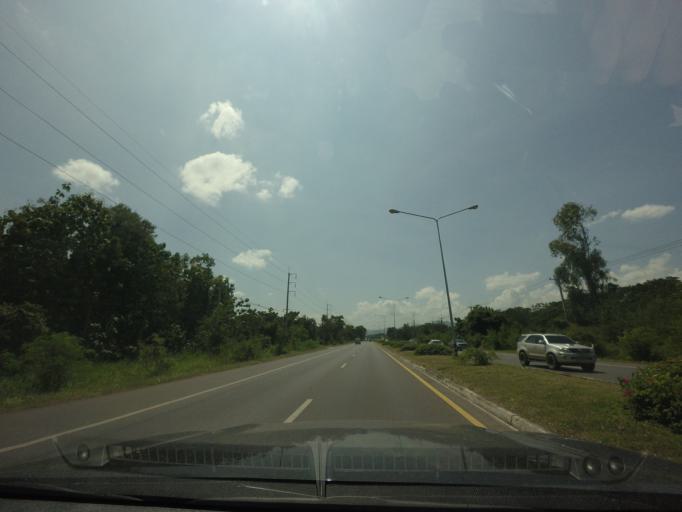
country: TH
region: Phetchabun
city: Lom Sak
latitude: 16.6935
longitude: 101.1687
